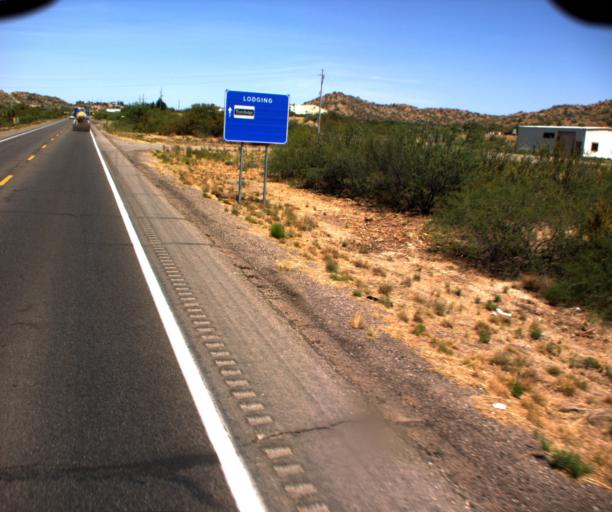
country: US
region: Arizona
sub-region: Gila County
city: Globe
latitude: 33.3709
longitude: -110.7303
